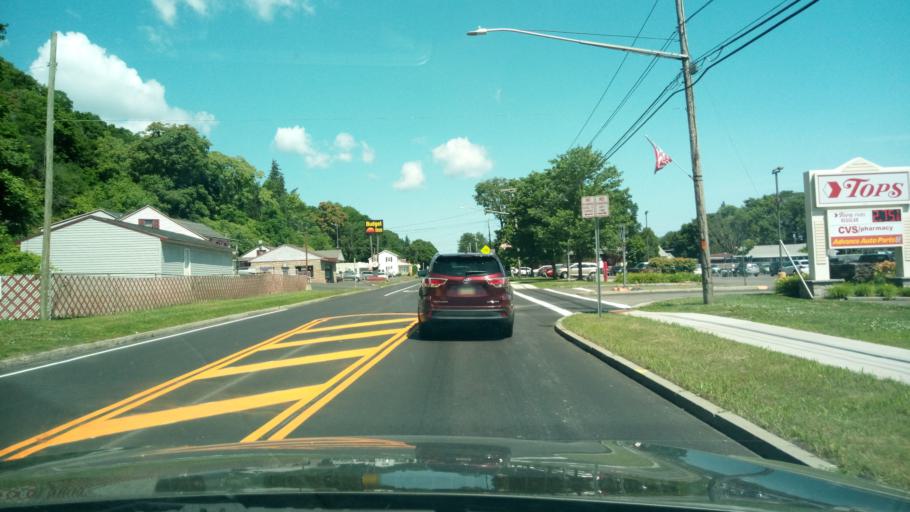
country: US
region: New York
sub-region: Schuyler County
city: Watkins Glen
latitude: 42.3690
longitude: -76.8673
